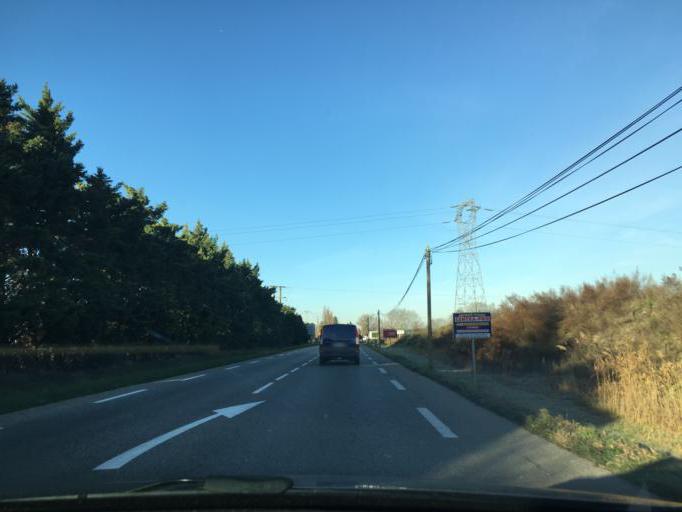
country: FR
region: Provence-Alpes-Cote d'Azur
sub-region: Departement du Vaucluse
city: L'Isle-sur-la-Sorgue
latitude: 43.8786
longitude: 5.0254
